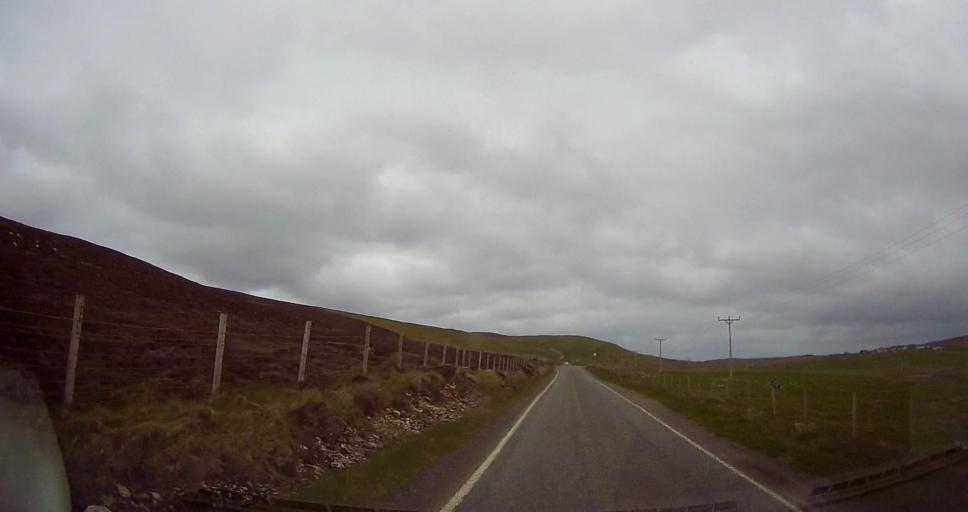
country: GB
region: Scotland
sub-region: Shetland Islands
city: Sandwick
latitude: 60.2447
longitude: -1.5113
